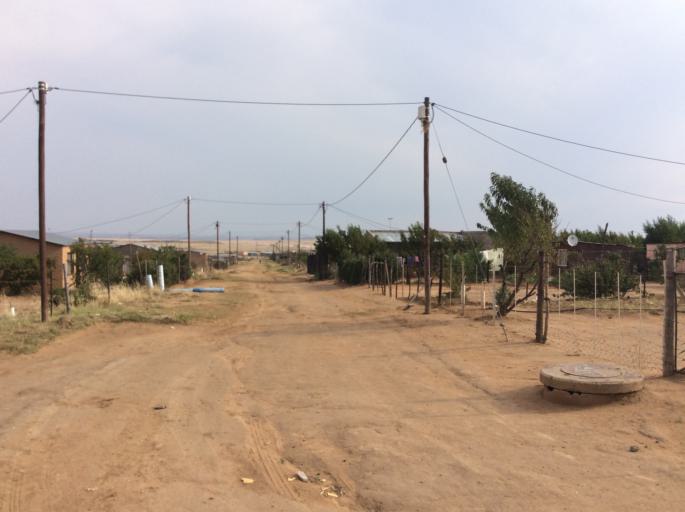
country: LS
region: Mafeteng
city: Mafeteng
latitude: -29.7086
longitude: 27.0155
